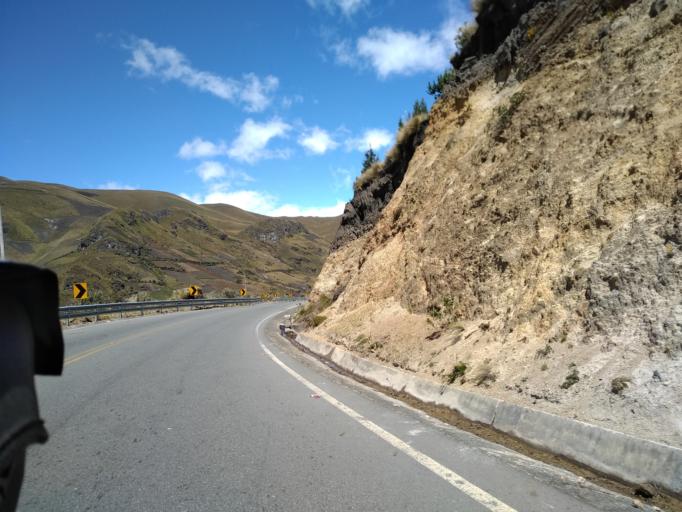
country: EC
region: Cotopaxi
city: Pujili
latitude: -0.9887
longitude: -78.9517
